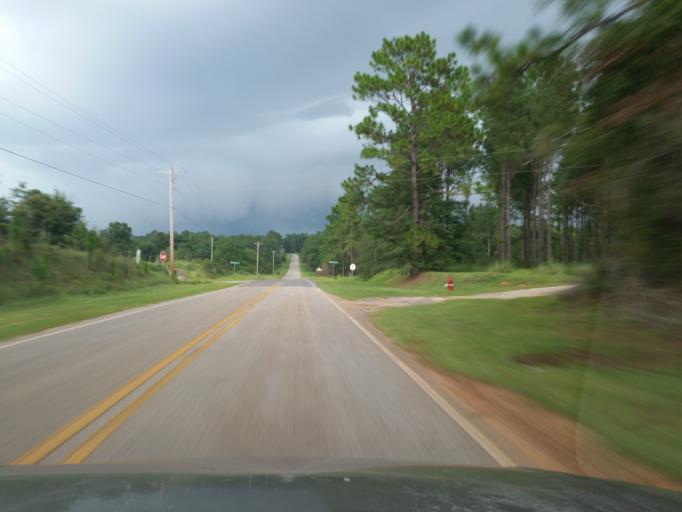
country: US
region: Alabama
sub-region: Baldwin County
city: Robertsdale
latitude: 30.5746
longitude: -87.5776
